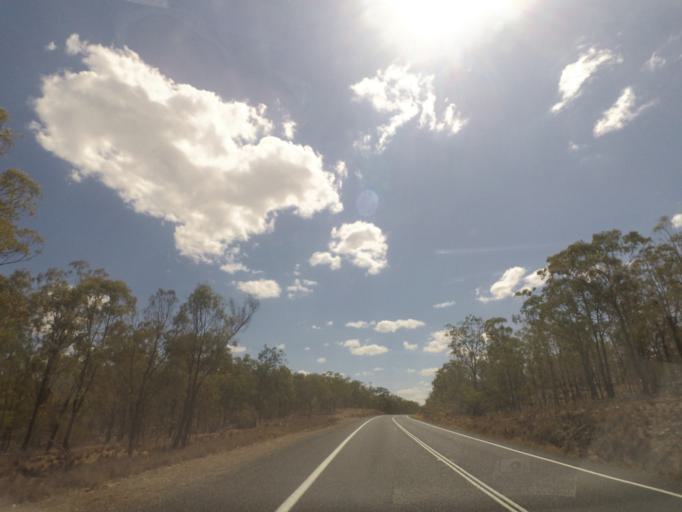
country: AU
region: Queensland
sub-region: Southern Downs
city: Warwick
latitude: -28.1626
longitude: 151.6821
